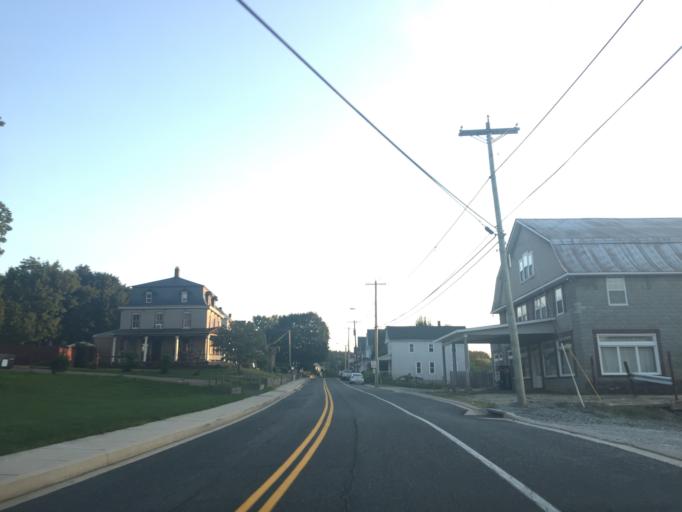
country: US
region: Pennsylvania
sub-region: York County
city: Susquehanna Trails
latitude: 39.7211
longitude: -76.3354
